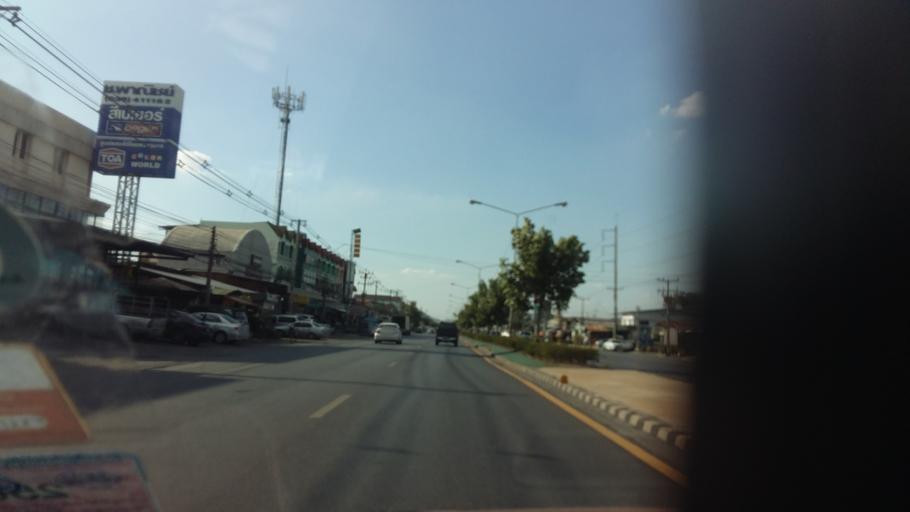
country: TH
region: Lop Buri
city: Lop Buri
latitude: 14.8208
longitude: 100.6483
